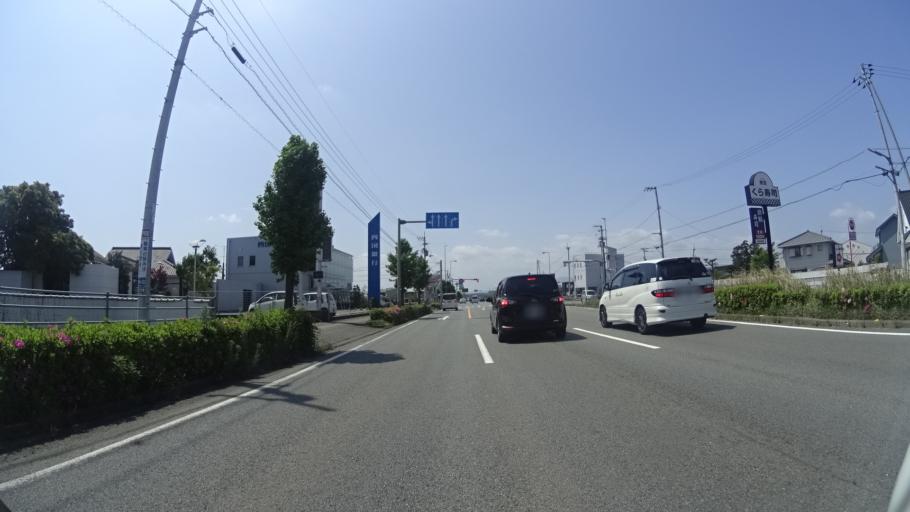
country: JP
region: Tokushima
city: Tokushima-shi
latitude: 34.1092
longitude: 134.5768
